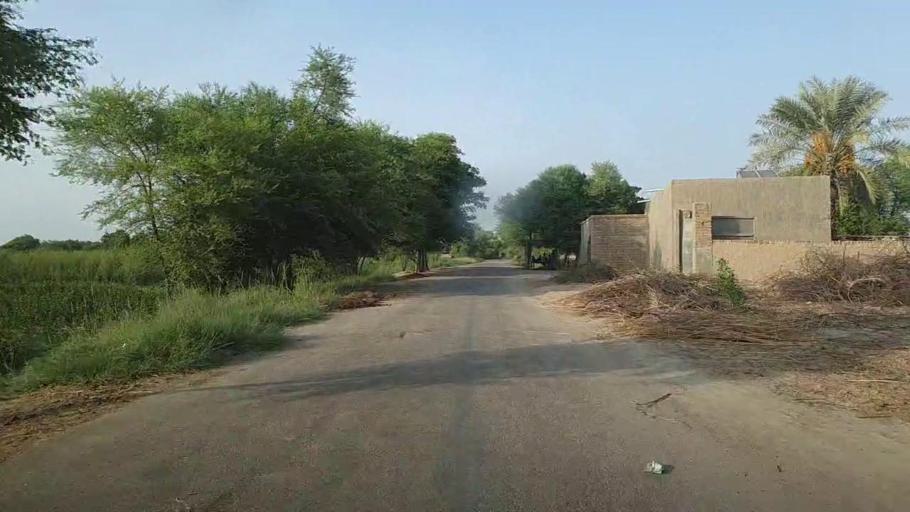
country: PK
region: Sindh
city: Ubauro
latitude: 28.1162
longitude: 69.8226
